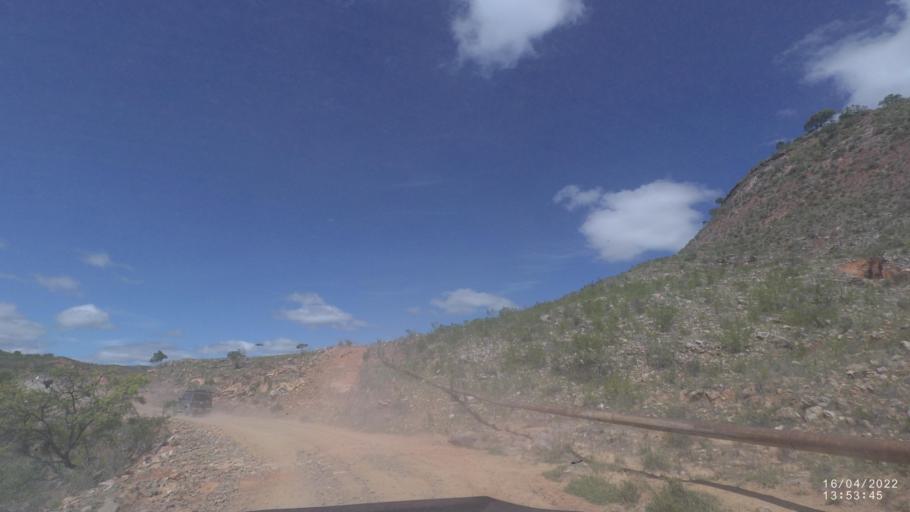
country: BO
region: Cochabamba
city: Mizque
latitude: -18.0252
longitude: -65.5695
